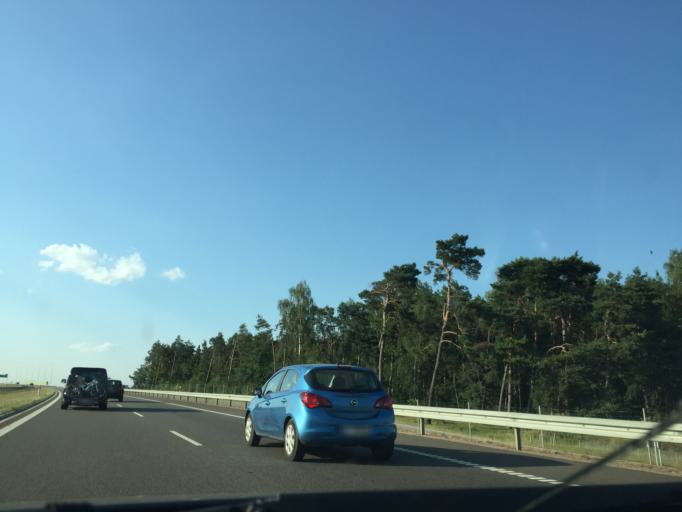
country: PL
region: Masovian Voivodeship
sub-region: Powiat radomski
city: Jedlinsk
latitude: 51.5259
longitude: 21.0840
